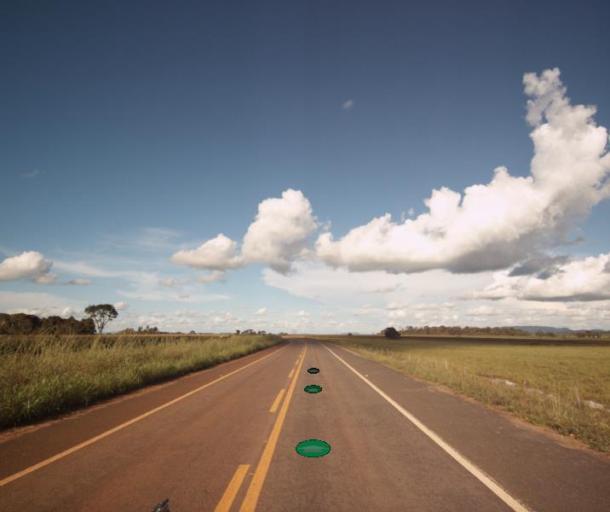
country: BR
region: Goias
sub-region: Itaberai
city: Itaberai
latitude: -15.9852
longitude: -49.6972
